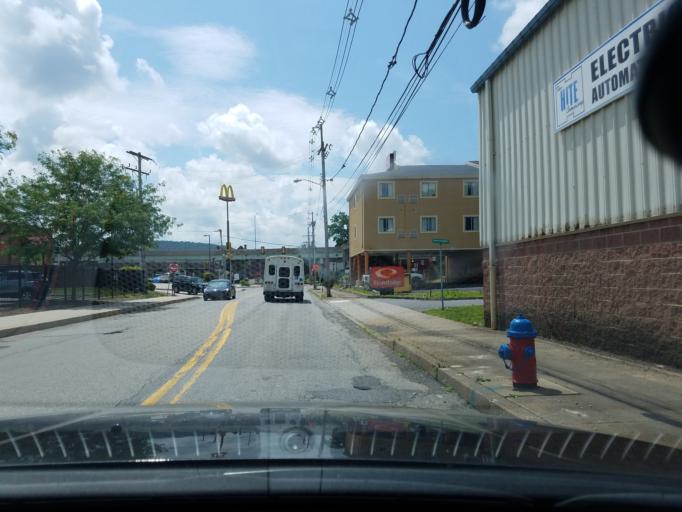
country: US
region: Pennsylvania
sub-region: Cambria County
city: Johnstown
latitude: 40.3216
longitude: -78.9204
